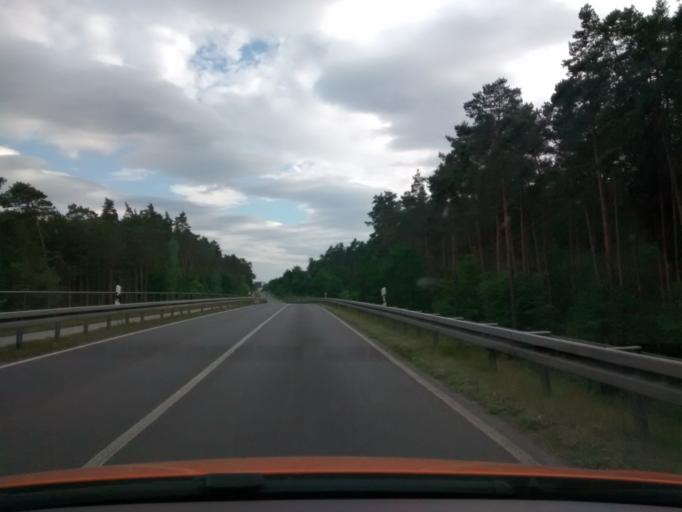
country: DE
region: Berlin
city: Bohnsdorf
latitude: 52.3852
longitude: 13.5686
